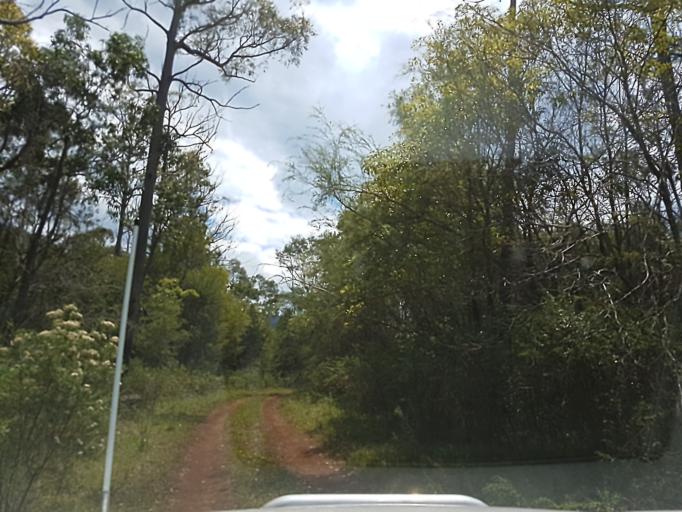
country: AU
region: Victoria
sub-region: East Gippsland
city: Lakes Entrance
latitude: -37.3582
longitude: 148.3566
